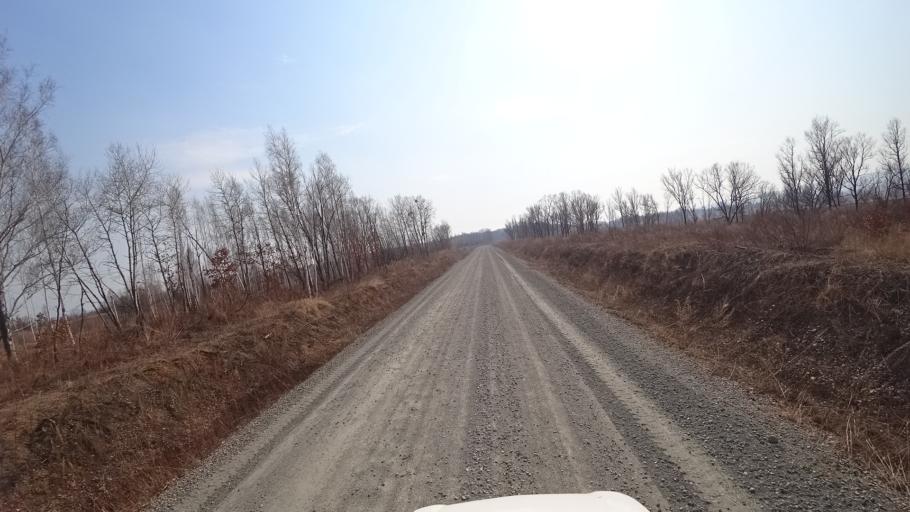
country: RU
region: Amur
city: Novobureyskiy
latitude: 49.8261
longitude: 129.9875
